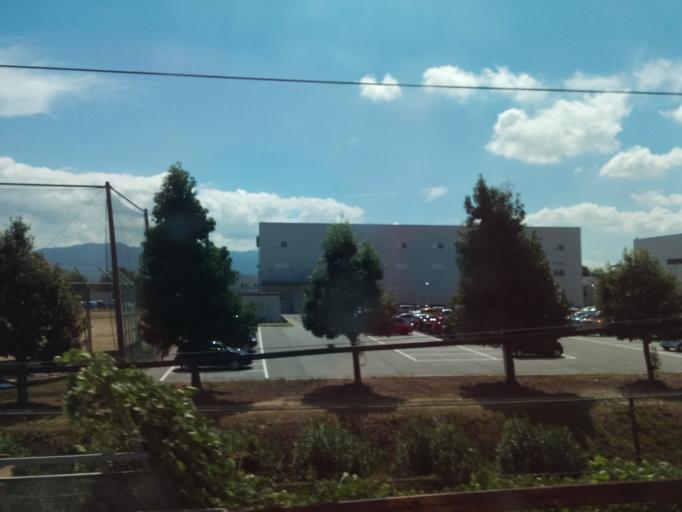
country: JP
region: Shiga Prefecture
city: Youkaichi
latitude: 35.1647
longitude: 136.2053
